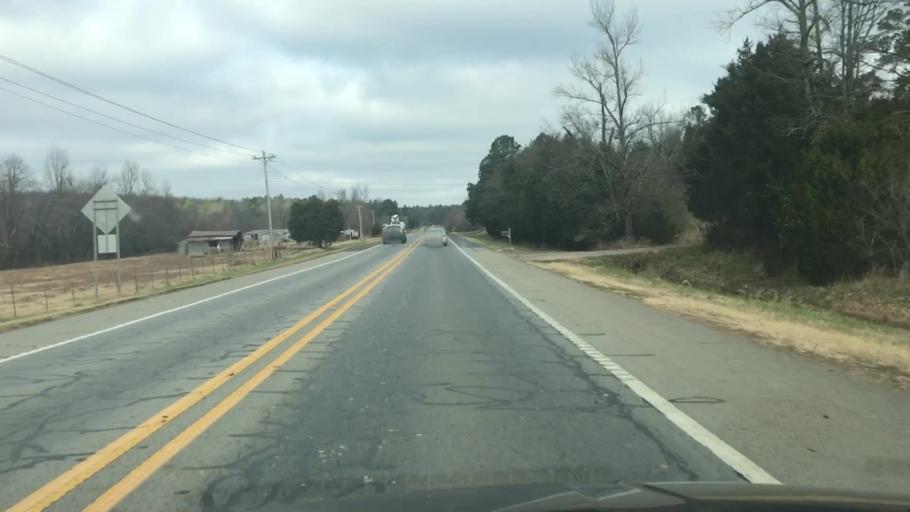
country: US
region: Arkansas
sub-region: Scott County
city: Waldron
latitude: 34.8273
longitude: -94.0392
